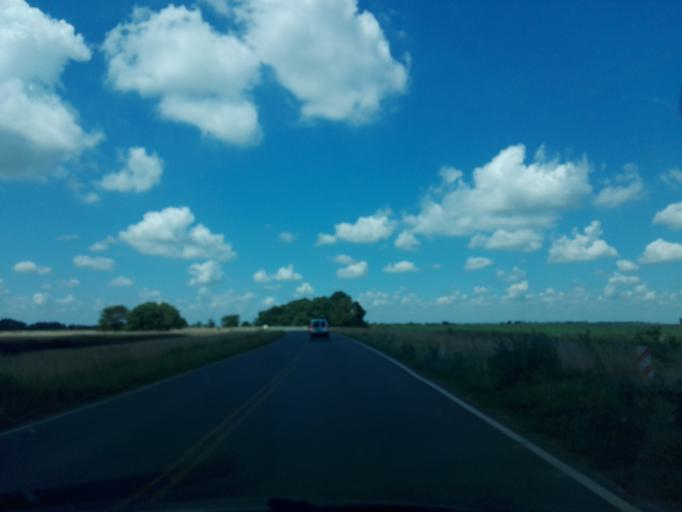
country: AR
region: Buenos Aires
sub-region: Partido de General Belgrano
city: General Belgrano
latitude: -35.8652
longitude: -58.6169
